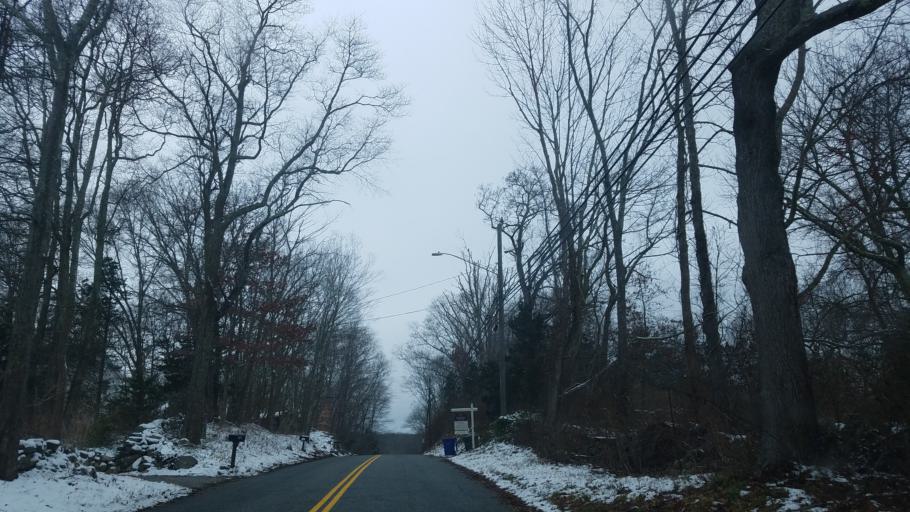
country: US
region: Connecticut
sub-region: New London County
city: Central Waterford
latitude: 41.3945
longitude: -72.1713
